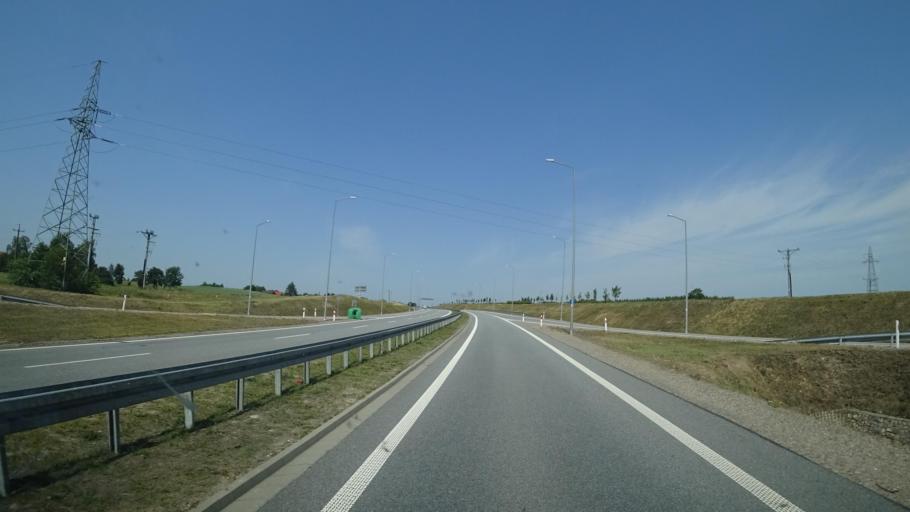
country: PL
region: Pomeranian Voivodeship
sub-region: Powiat koscierski
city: Koscierzyna
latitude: 54.1246
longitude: 18.0192
